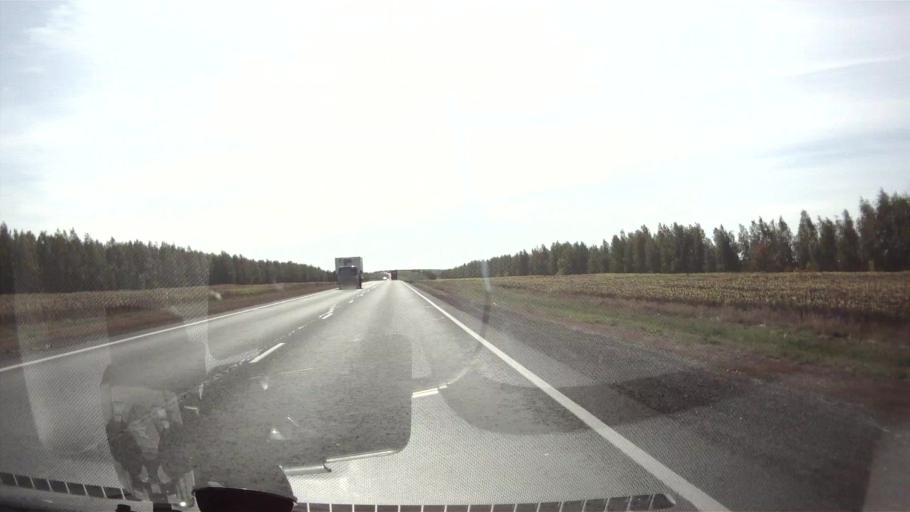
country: RU
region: Samara
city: Syzran'
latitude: 52.9081
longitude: 48.2987
